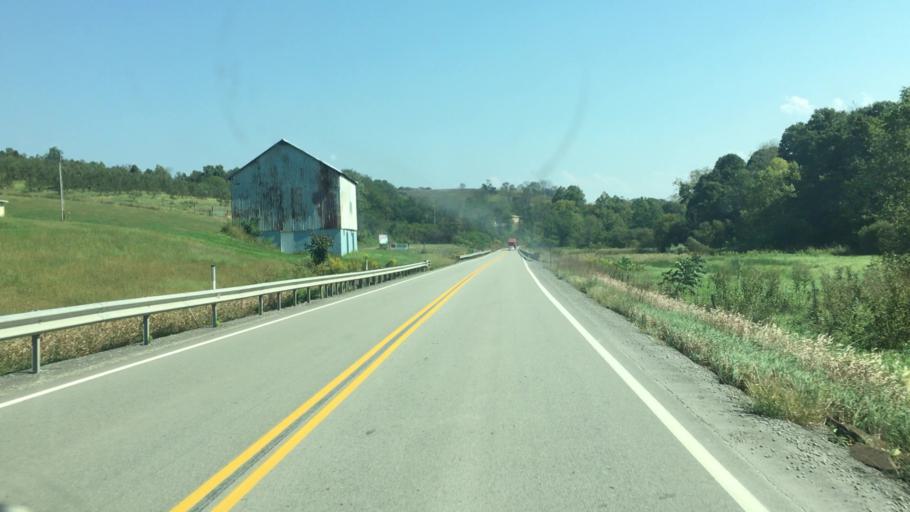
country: US
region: Pennsylvania
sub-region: Washington County
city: Washington
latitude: 40.0295
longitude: -80.3143
